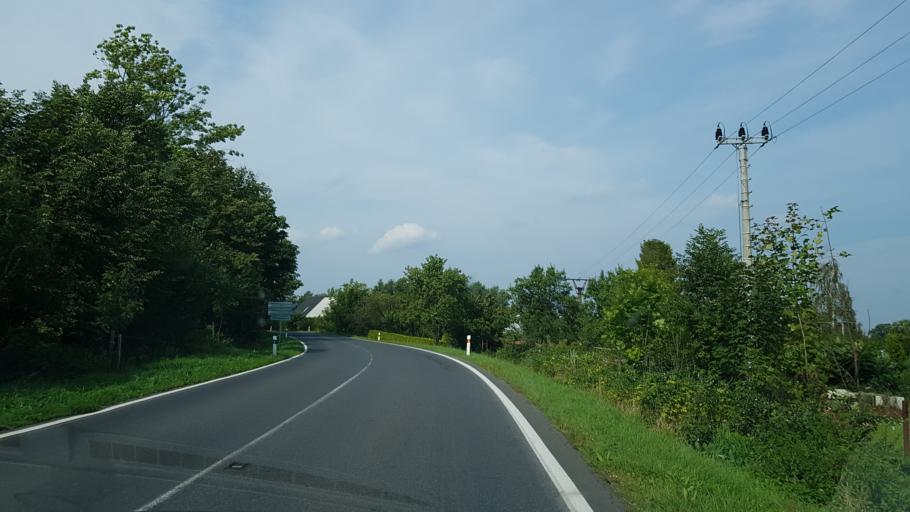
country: CZ
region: Olomoucky
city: Zlate Hory
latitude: 50.2560
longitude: 17.3787
